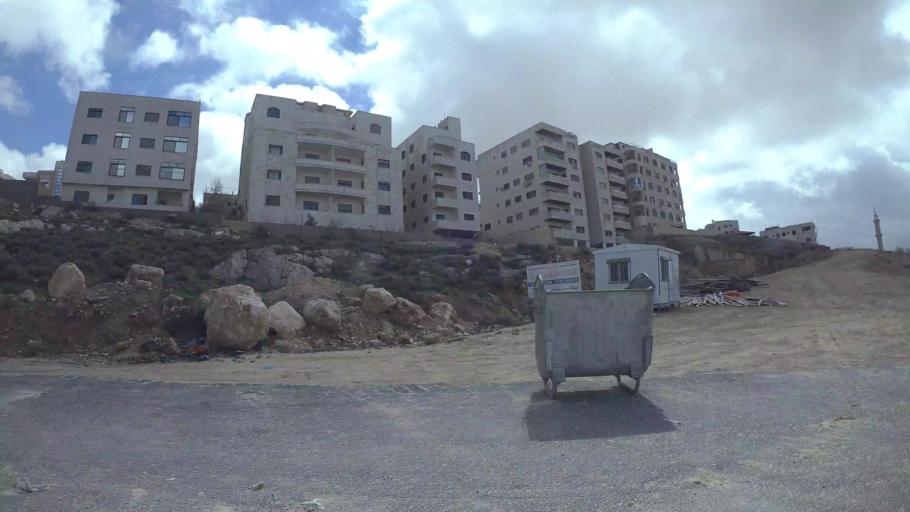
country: JO
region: Amman
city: Al Jubayhah
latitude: 32.0643
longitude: 35.8713
